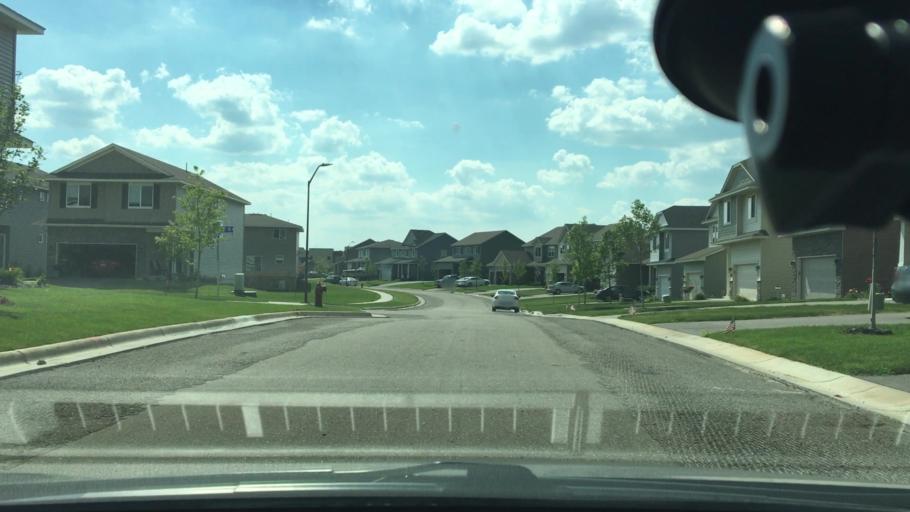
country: US
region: Minnesota
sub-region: Hennepin County
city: New Hope
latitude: 45.0540
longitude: -93.3813
